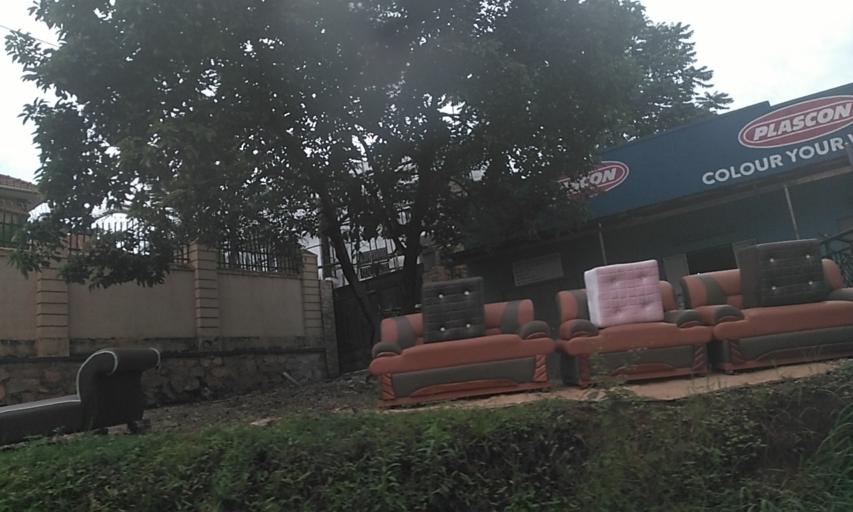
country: UG
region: Central Region
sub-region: Wakiso District
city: Kireka
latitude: 0.3750
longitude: 32.6437
